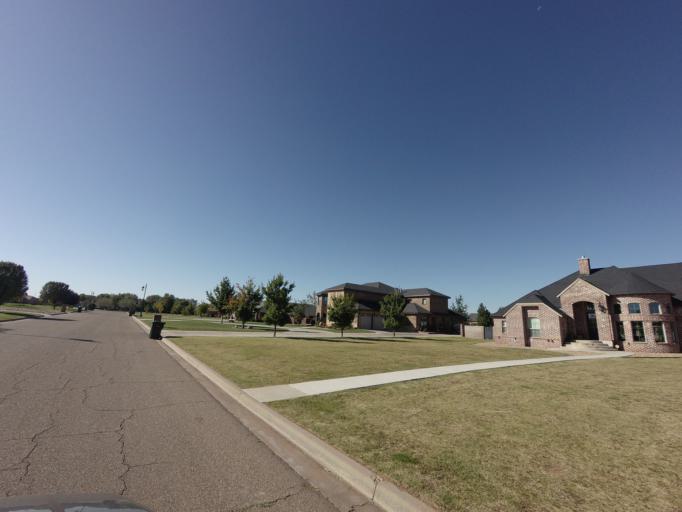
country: US
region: New Mexico
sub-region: Curry County
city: Clovis
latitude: 34.4327
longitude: -103.1675
